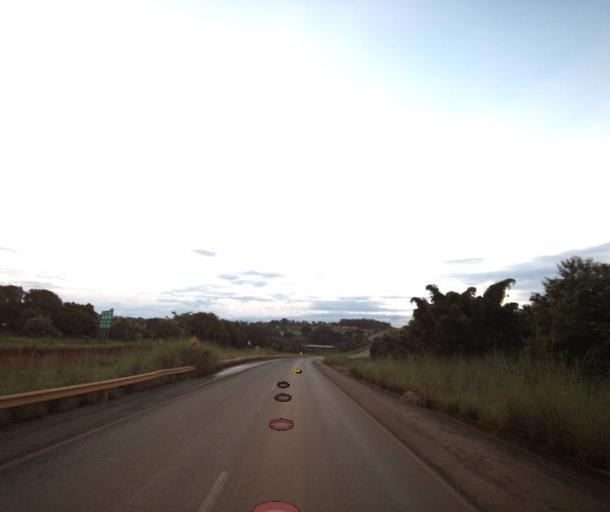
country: BR
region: Goias
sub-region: Anapolis
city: Anapolis
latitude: -16.2467
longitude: -49.0002
